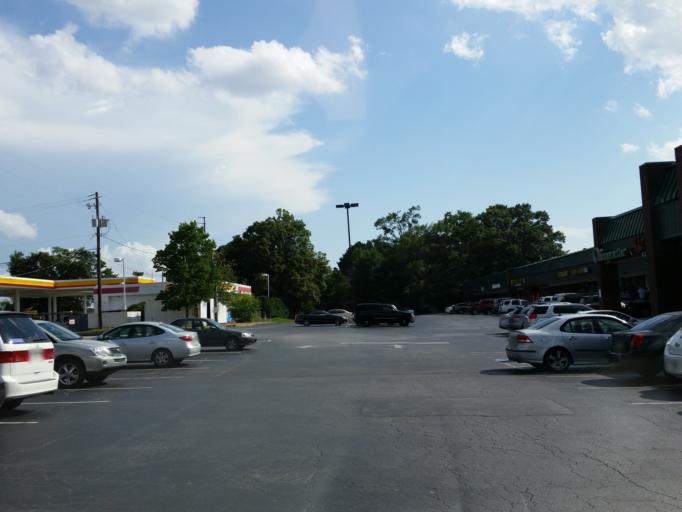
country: US
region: Georgia
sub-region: Cobb County
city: Marietta
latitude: 34.0173
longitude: -84.4932
